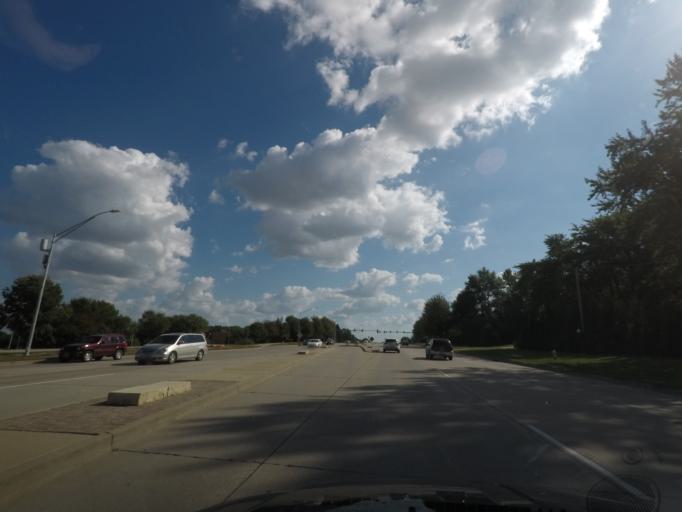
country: US
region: Iowa
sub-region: Dallas County
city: Waukee
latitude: 41.5816
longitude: -93.8092
